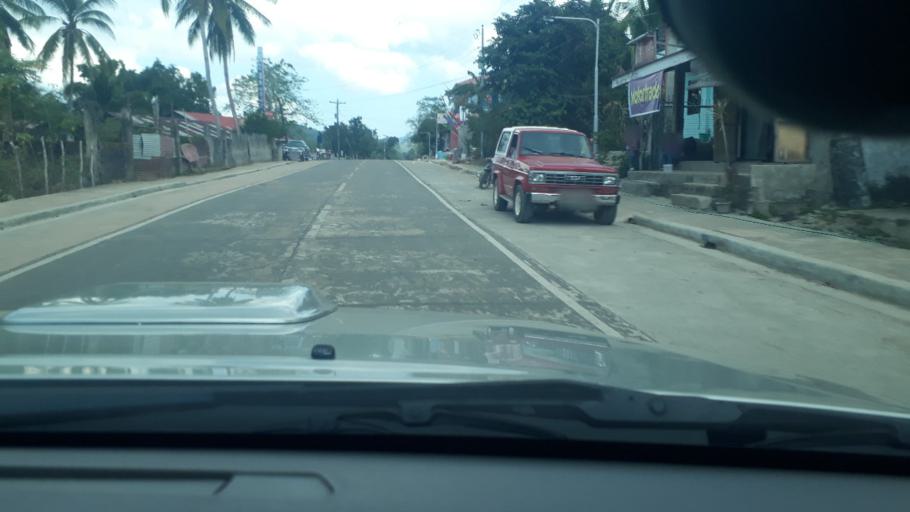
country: PH
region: Mimaropa
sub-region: Province of Palawan
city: Salvacion
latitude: 12.1309
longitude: 119.9373
